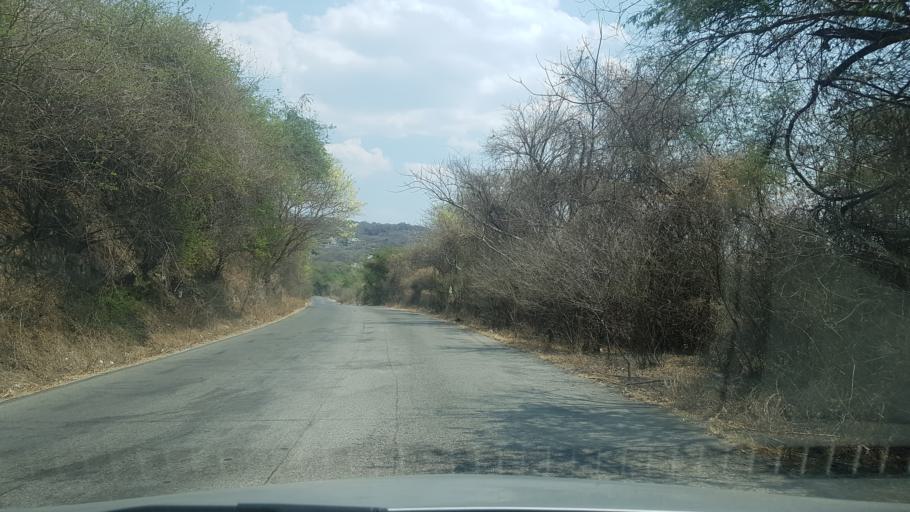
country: MX
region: Morelos
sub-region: Tlaltizapan de Zapata
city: Colonia Palo Prieto (Chipitongo)
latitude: 18.7489
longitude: -99.1136
